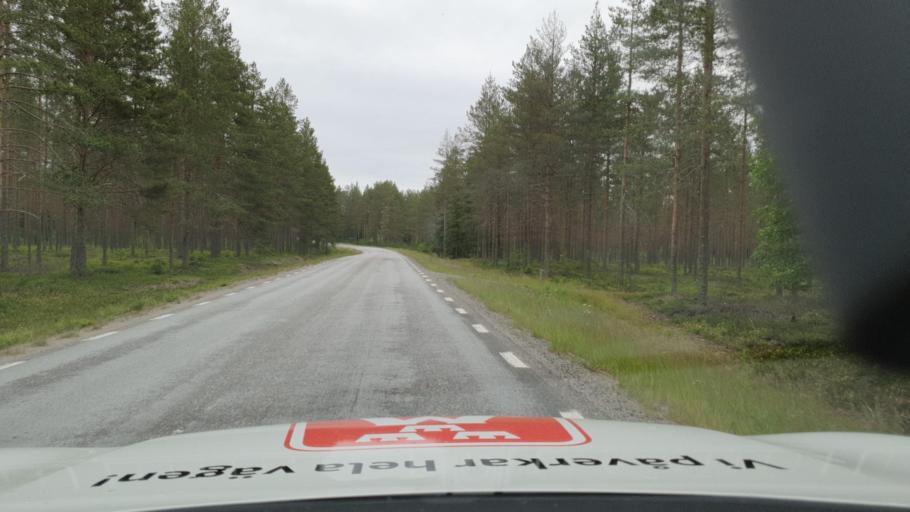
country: SE
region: Vaesterbotten
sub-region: Nordmalings Kommun
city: Nordmaling
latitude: 63.6075
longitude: 19.4197
